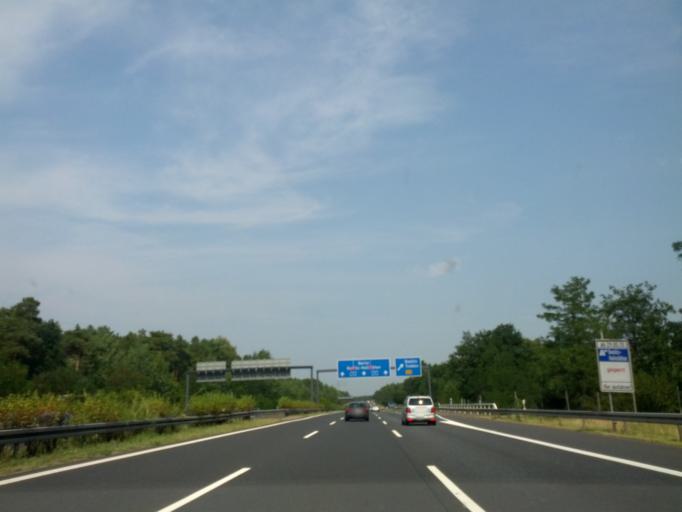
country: DE
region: Brandenburg
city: Borkheide
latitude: 52.2150
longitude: 12.8994
